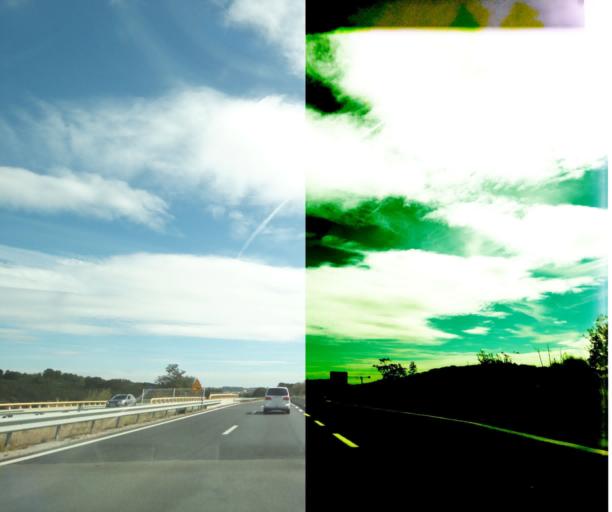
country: FR
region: Languedoc-Roussillon
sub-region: Departement de l'Herault
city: Grabels
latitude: 43.6259
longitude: 3.7850
